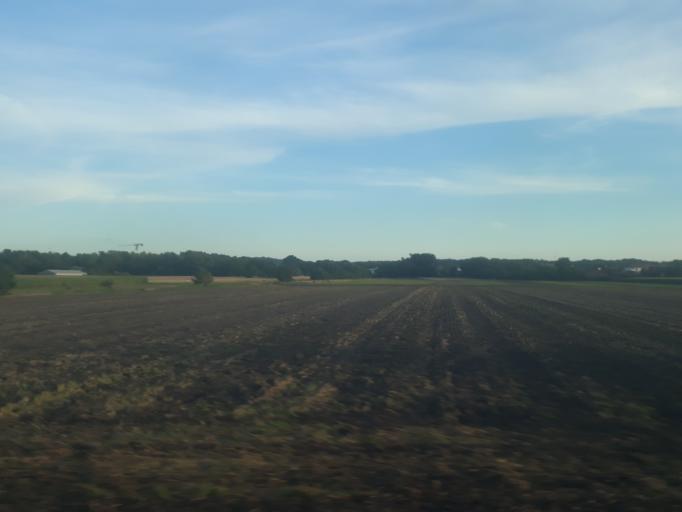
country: DE
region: Lower Saxony
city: Neu Wulmstorf
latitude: 53.4739
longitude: 9.8045
